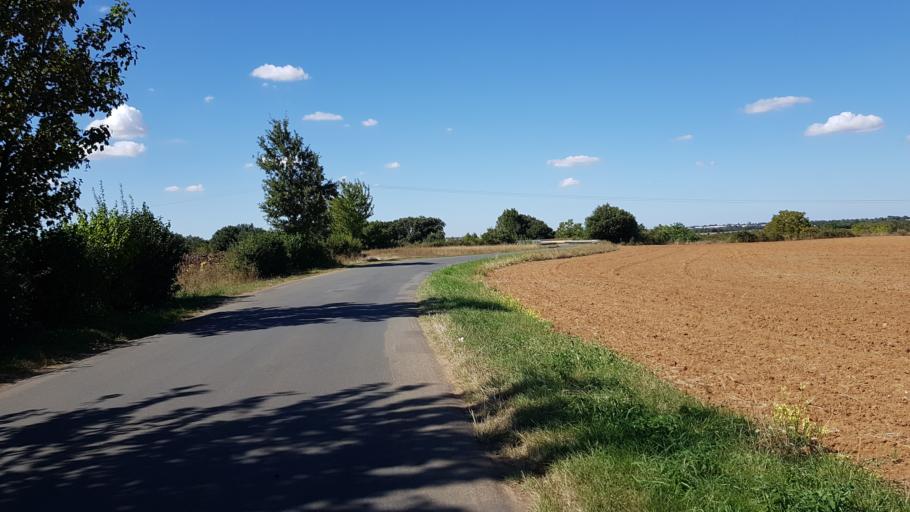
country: FR
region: Poitou-Charentes
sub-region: Departement des Deux-Sevres
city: Vouille
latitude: 46.3112
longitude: -0.3508
